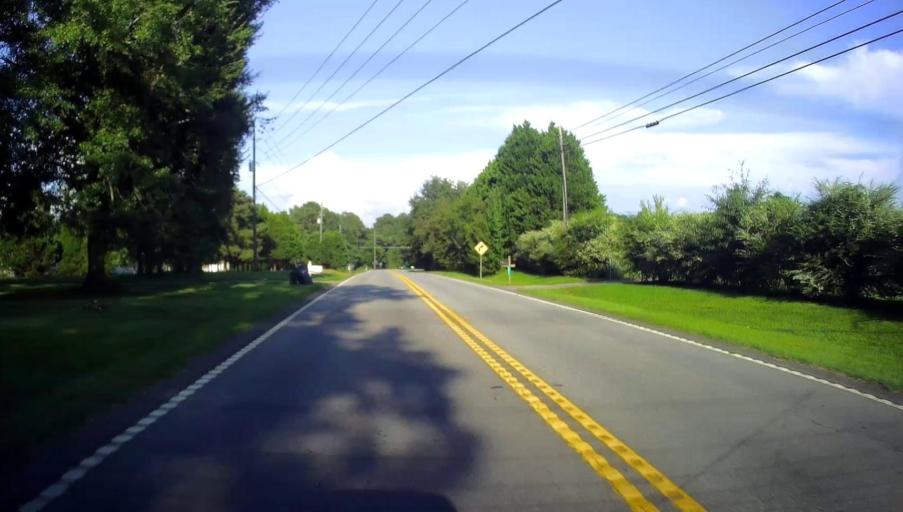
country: US
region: Georgia
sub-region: Houston County
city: Perry
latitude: 32.5029
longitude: -83.6283
